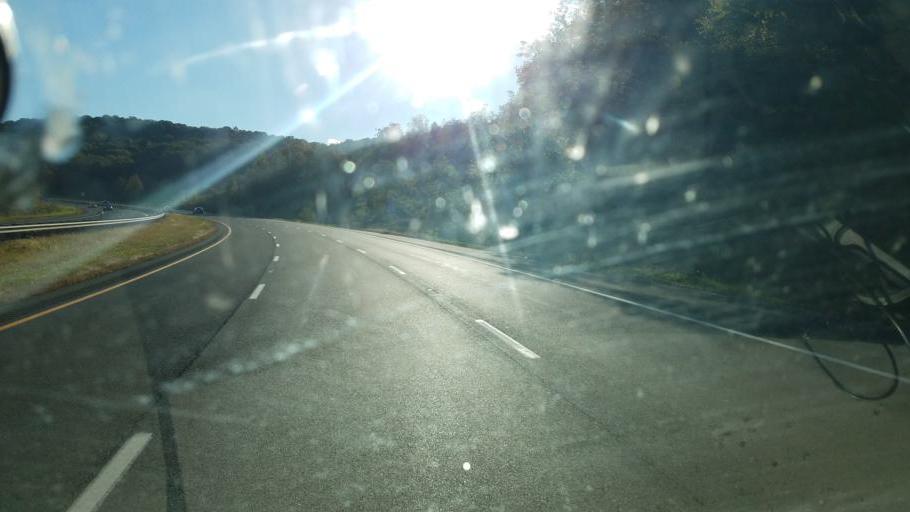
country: US
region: Maryland
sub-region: Allegany County
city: Cumberland
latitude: 39.6694
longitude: -78.7040
